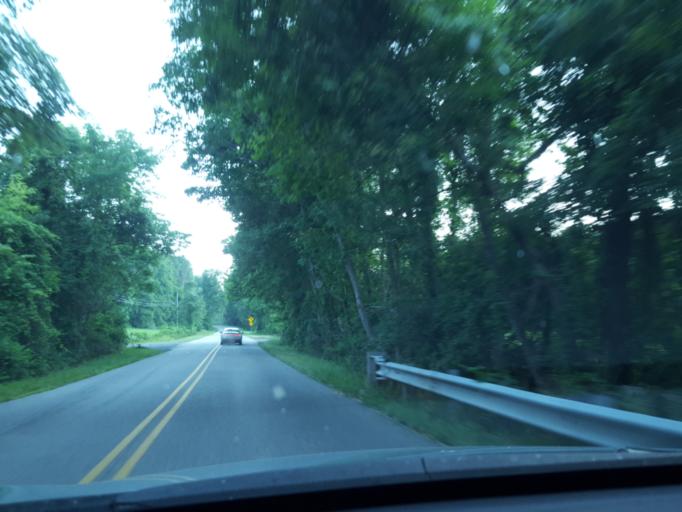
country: US
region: Virginia
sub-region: Augusta County
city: Lyndhurst
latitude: 37.9402
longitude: -78.9683
